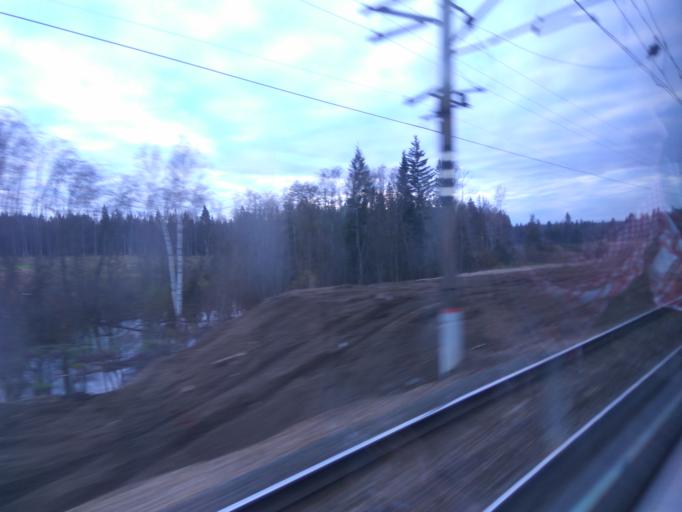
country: RU
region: Moskovskaya
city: Selyatino
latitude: 55.5113
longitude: 36.9585
